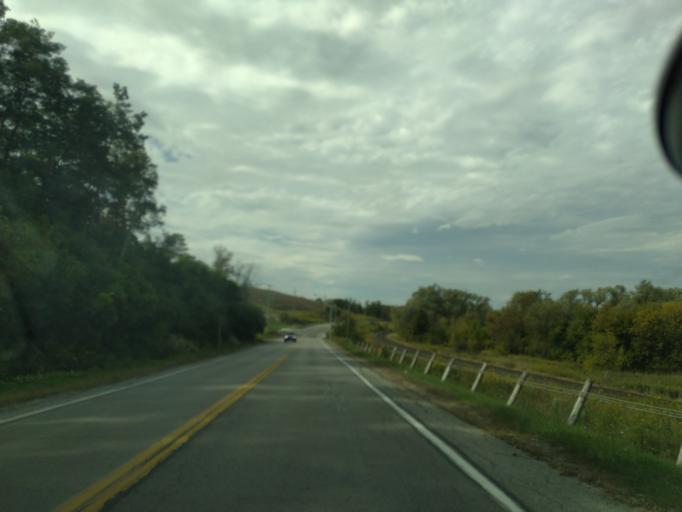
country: CA
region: Ontario
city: Newmarket
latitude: 44.0934
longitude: -79.4913
